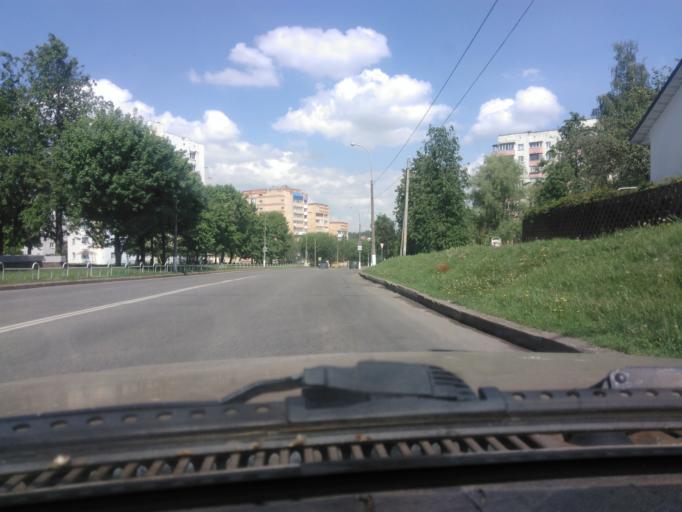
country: BY
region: Mogilev
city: Mahilyow
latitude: 53.9194
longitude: 30.3118
